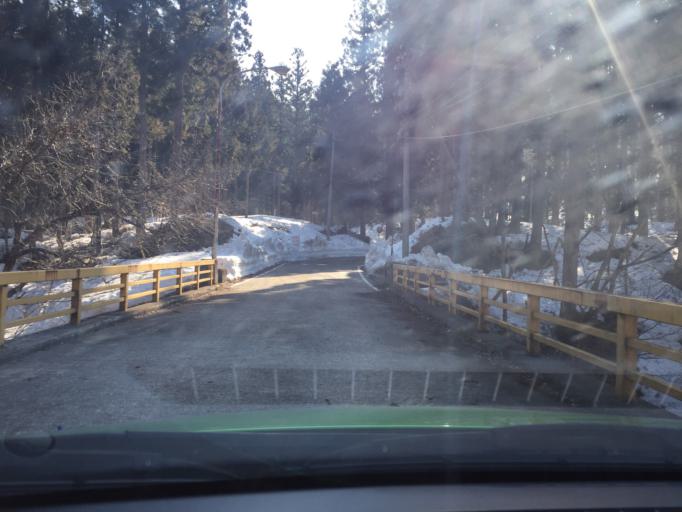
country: JP
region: Ishikawa
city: Tsurugi-asahimachi
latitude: 36.2746
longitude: 136.6962
